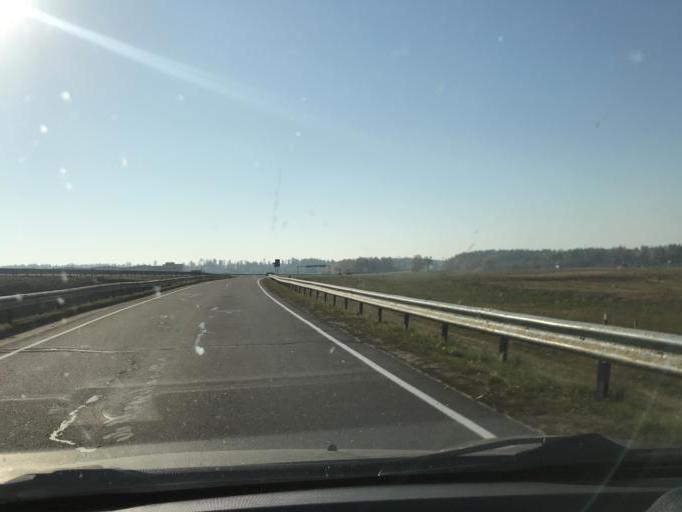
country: BY
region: Minsk
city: Pryvol'ny
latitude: 53.8038
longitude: 27.7888
